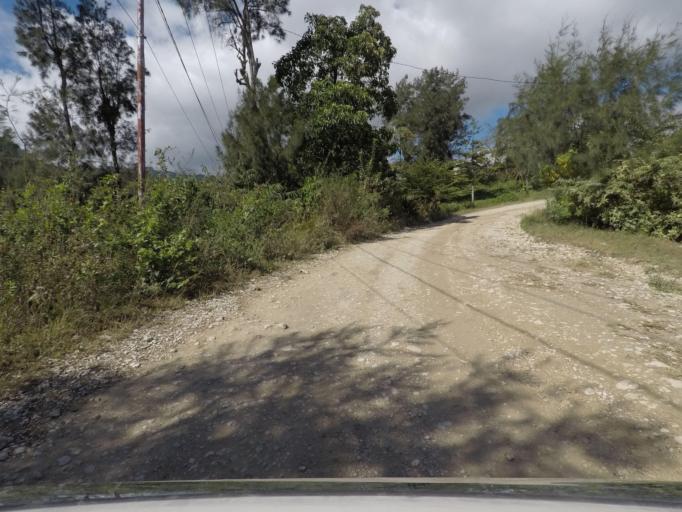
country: TL
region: Baucau
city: Venilale
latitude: -8.6762
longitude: 126.3715
